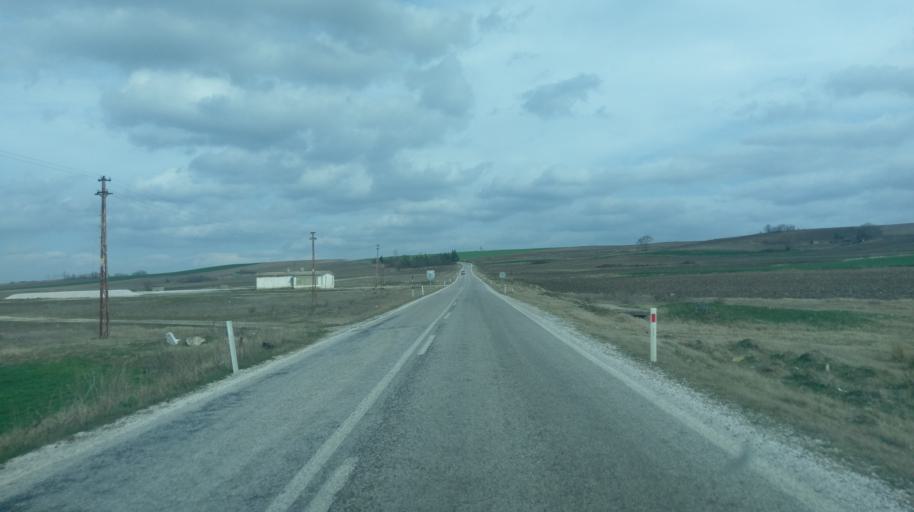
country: TR
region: Edirne
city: Haskoy
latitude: 41.6442
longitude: 26.8701
